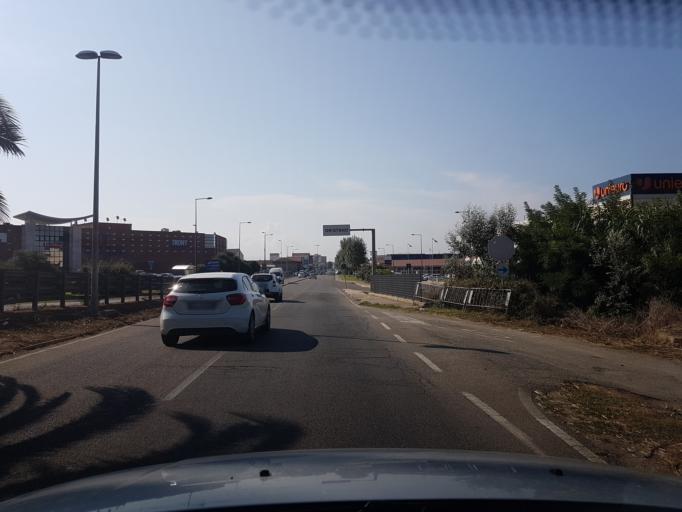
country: IT
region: Sardinia
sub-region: Provincia di Oristano
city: Oristano
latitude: 39.9166
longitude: 8.5844
